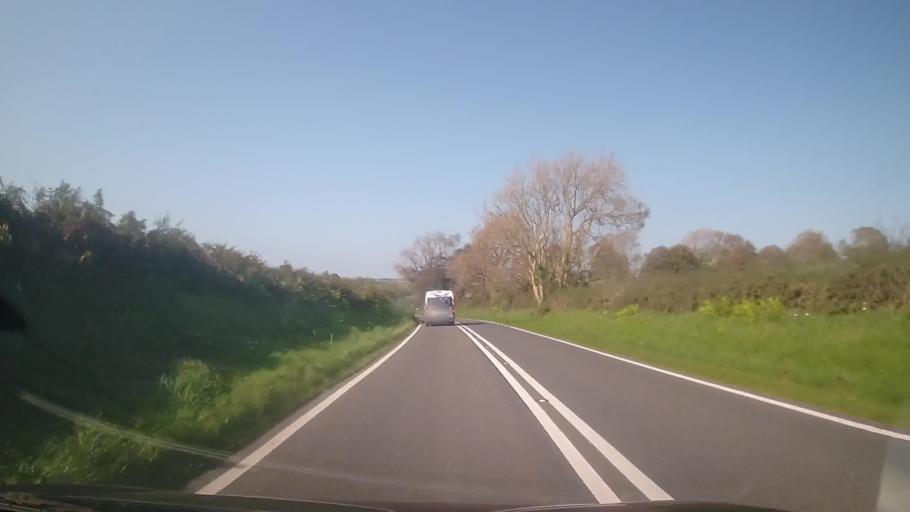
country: GB
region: Wales
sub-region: County of Ceredigion
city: Cardigan
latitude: 52.0338
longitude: -4.6945
